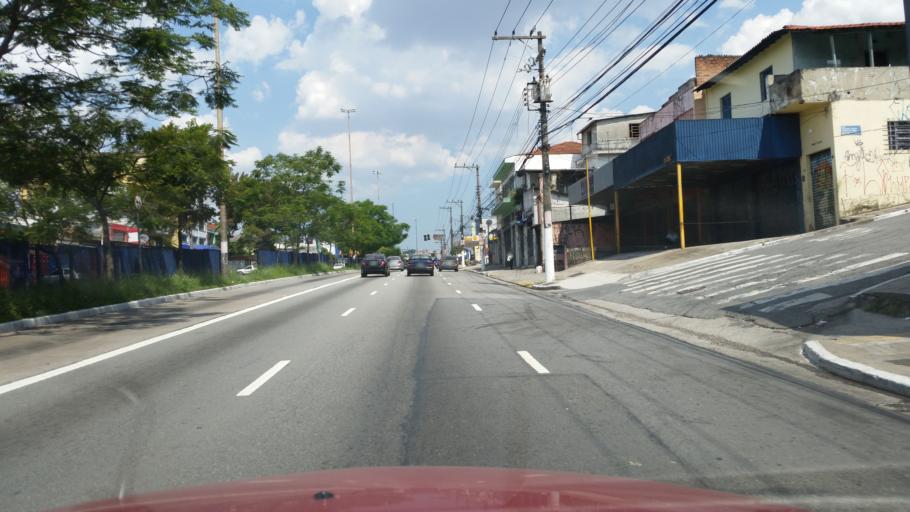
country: BR
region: Sao Paulo
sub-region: Diadema
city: Diadema
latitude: -23.6685
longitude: -46.6513
